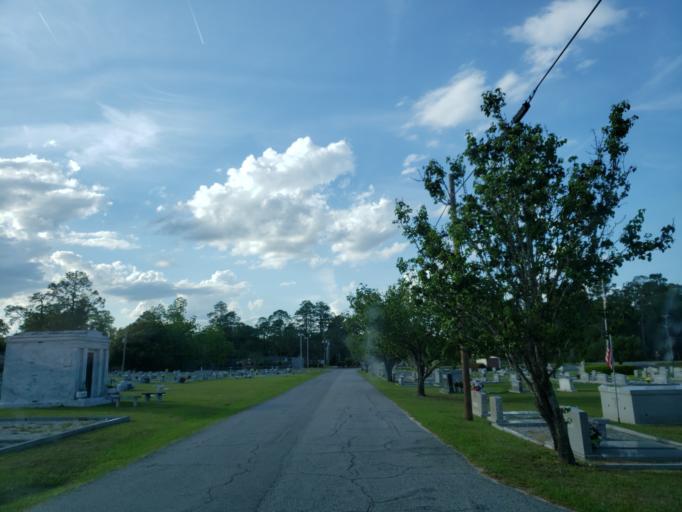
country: US
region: Georgia
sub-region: Cook County
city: Adel
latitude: 31.1372
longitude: -83.4177
